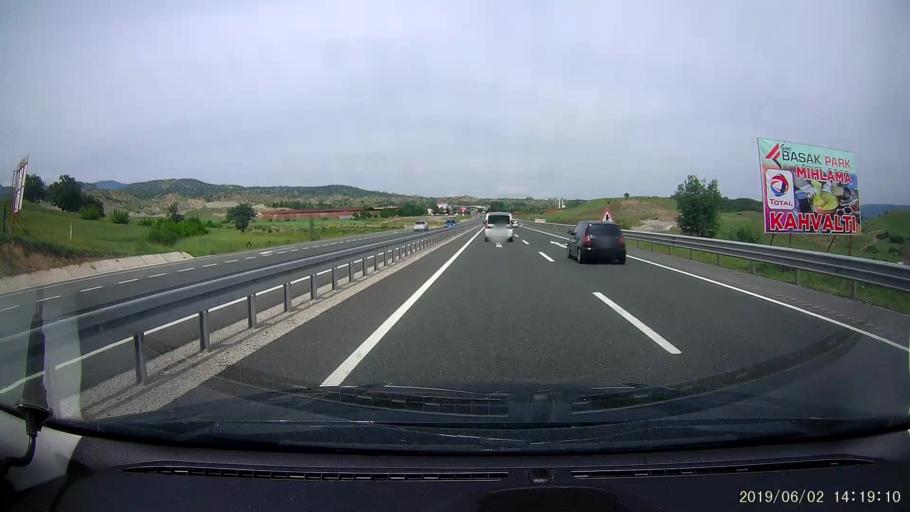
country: TR
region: Kastamonu
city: Tosya
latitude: 40.9618
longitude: 33.9715
